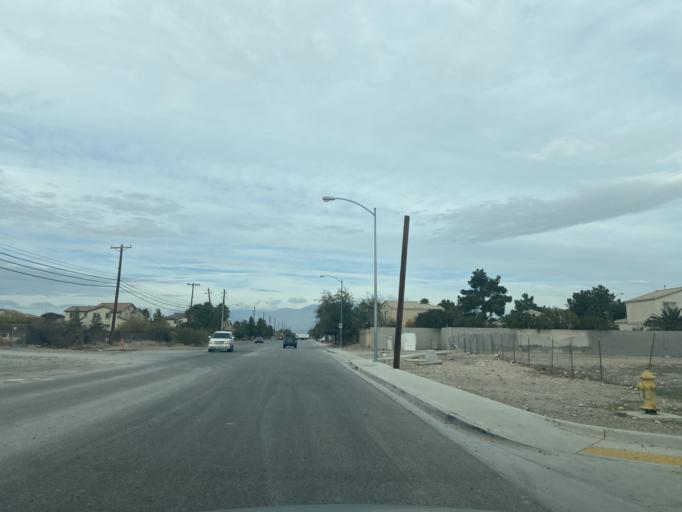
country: US
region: Nevada
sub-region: Clark County
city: Las Vegas
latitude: 36.2183
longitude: -115.1884
